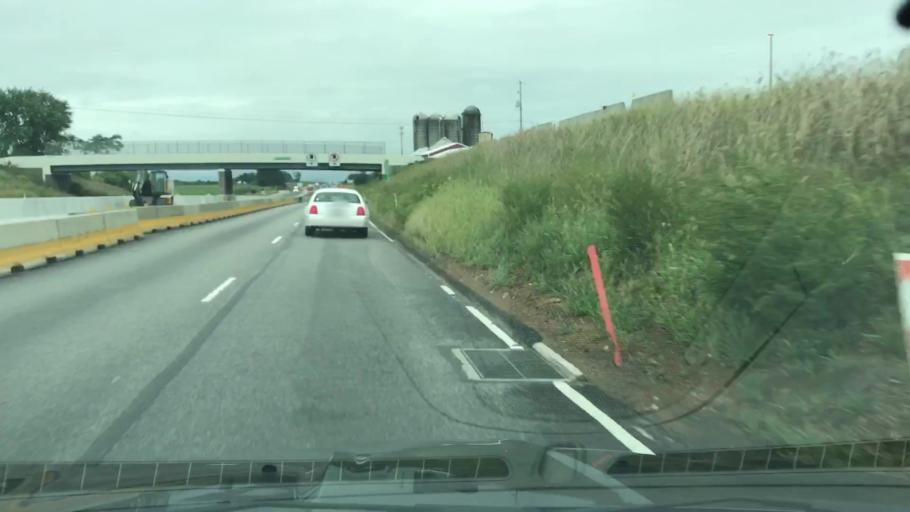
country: US
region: Pennsylvania
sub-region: Cumberland County
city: Shippensburg
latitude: 40.1705
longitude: -77.5656
